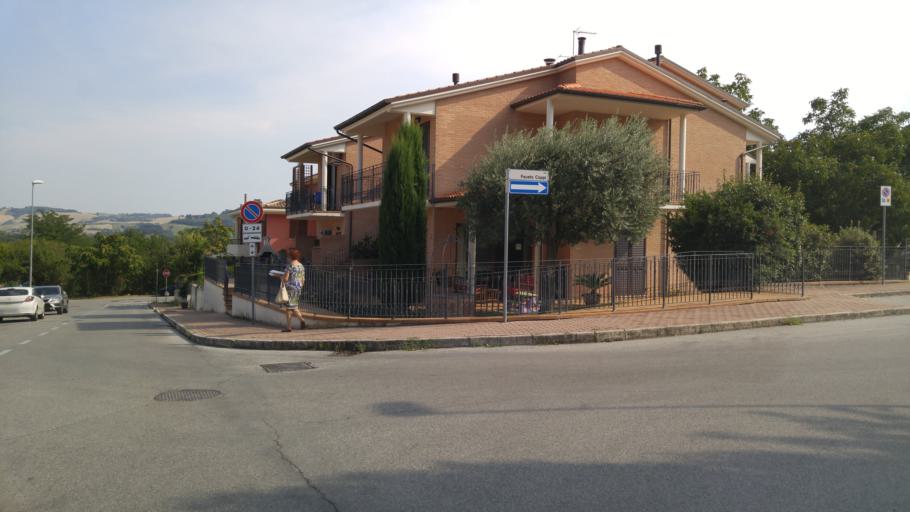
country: IT
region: The Marches
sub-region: Provincia di Pesaro e Urbino
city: Calcinelli
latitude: 43.7468
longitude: 12.9107
